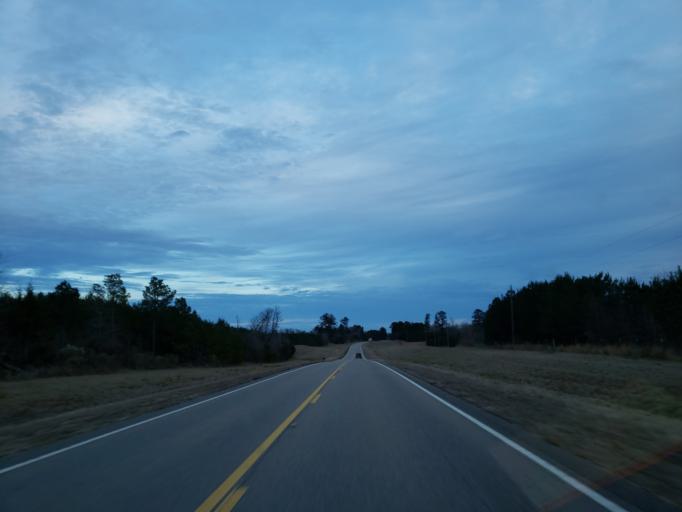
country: US
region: Mississippi
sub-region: Kemper County
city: De Kalb
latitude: 32.8309
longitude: -88.3706
